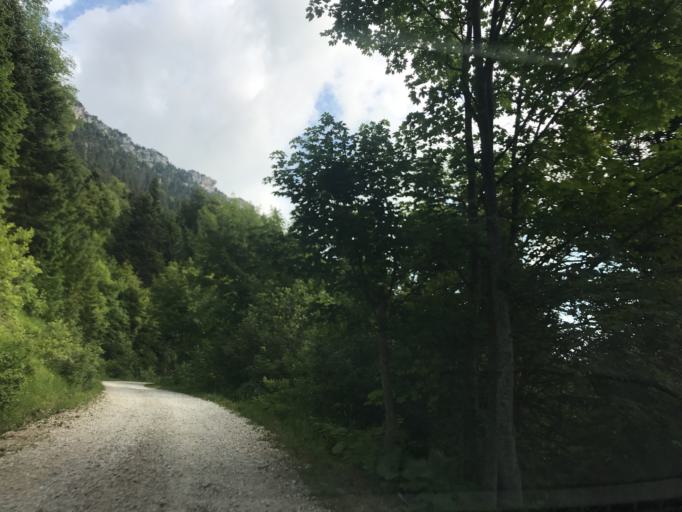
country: FR
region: Rhone-Alpes
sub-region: Departement de l'Isere
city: Barraux
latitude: 45.4186
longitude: 5.9374
